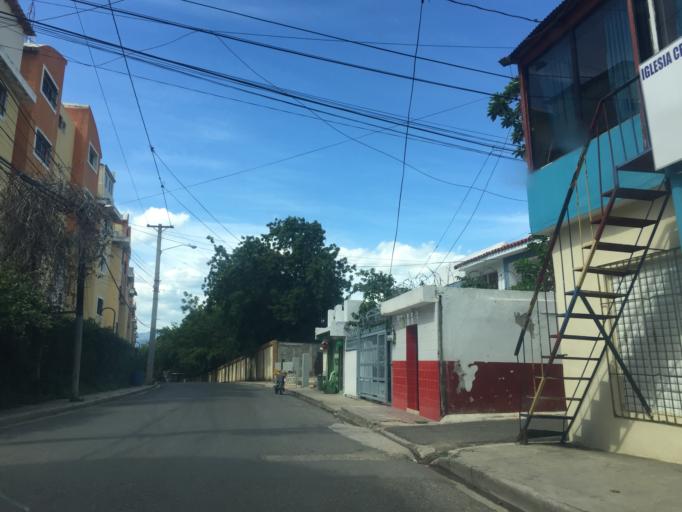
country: DO
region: Santiago
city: Santiago de los Caballeros
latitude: 19.4344
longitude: -70.6804
